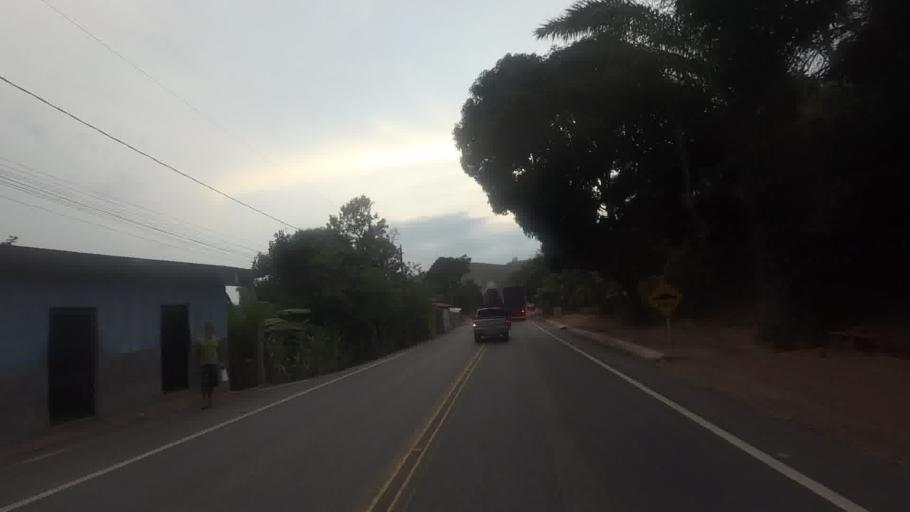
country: BR
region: Rio de Janeiro
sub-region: Carmo
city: Carmo
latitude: -21.8180
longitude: -42.5997
